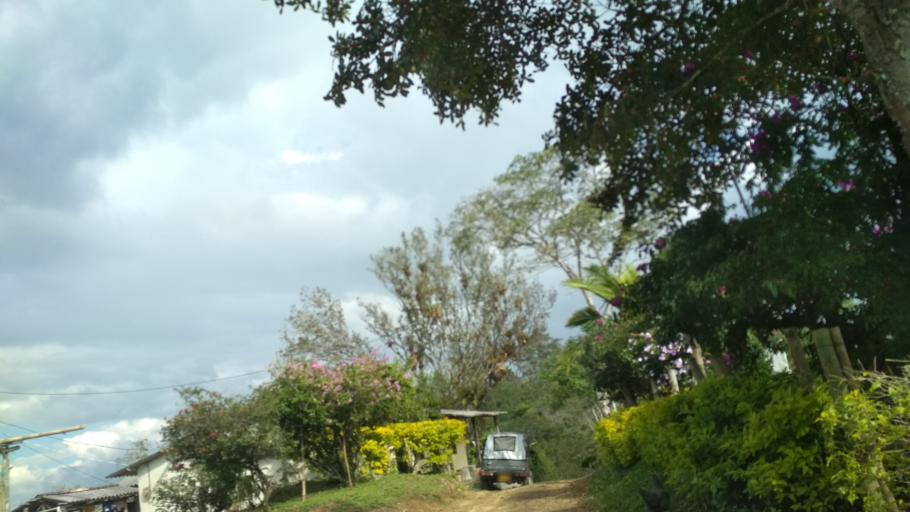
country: CO
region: Cauca
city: Lopez
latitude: 2.4015
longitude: -76.7122
